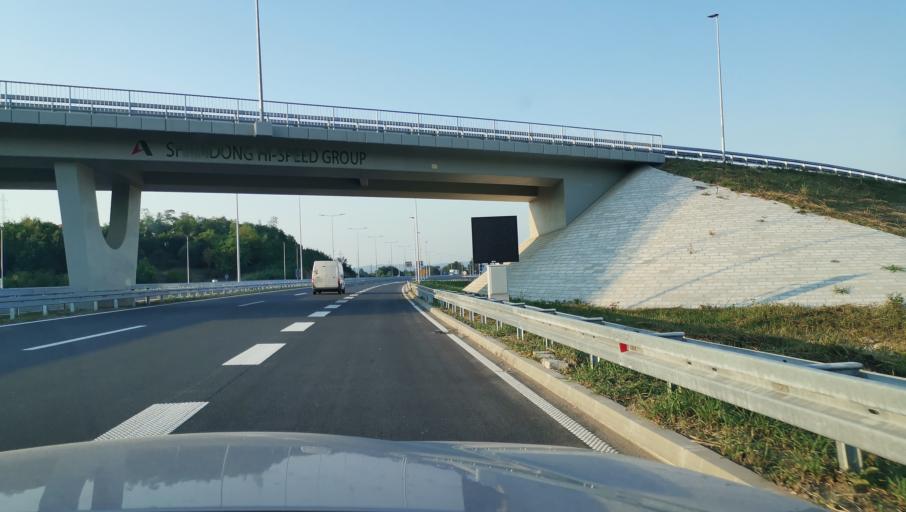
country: RS
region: Central Serbia
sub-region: Kolubarski Okrug
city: Ljig
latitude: 44.2325
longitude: 20.2543
